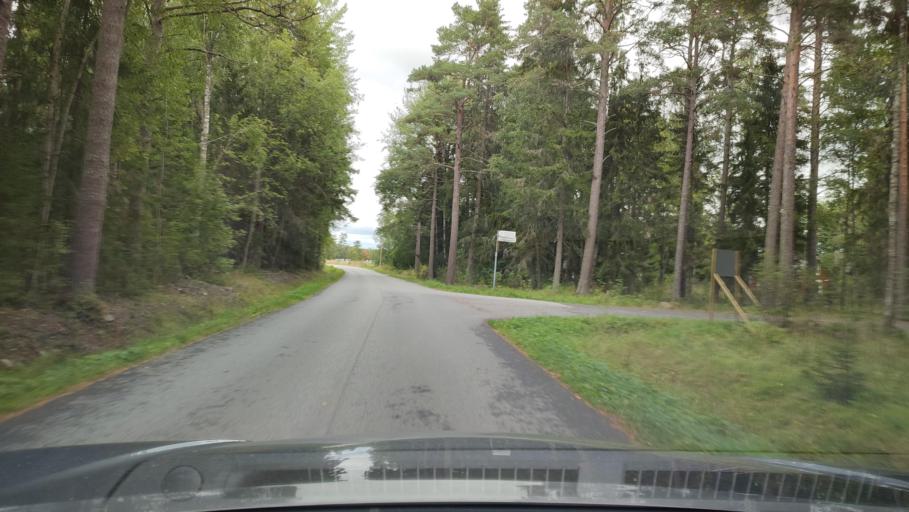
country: FI
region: Ostrobothnia
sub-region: Sydosterbotten
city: Kristinestad
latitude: 62.2579
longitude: 21.3576
